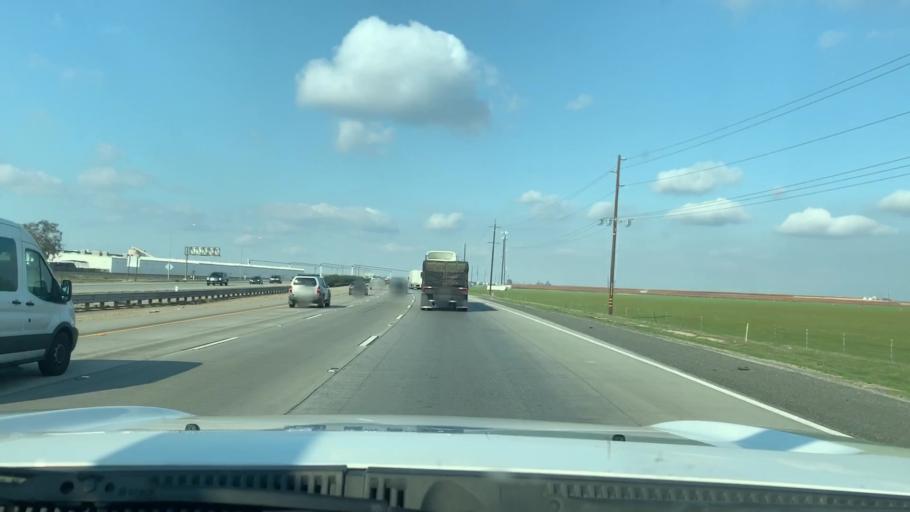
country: US
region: California
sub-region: Kern County
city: Shafter
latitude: 35.5601
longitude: -119.1976
